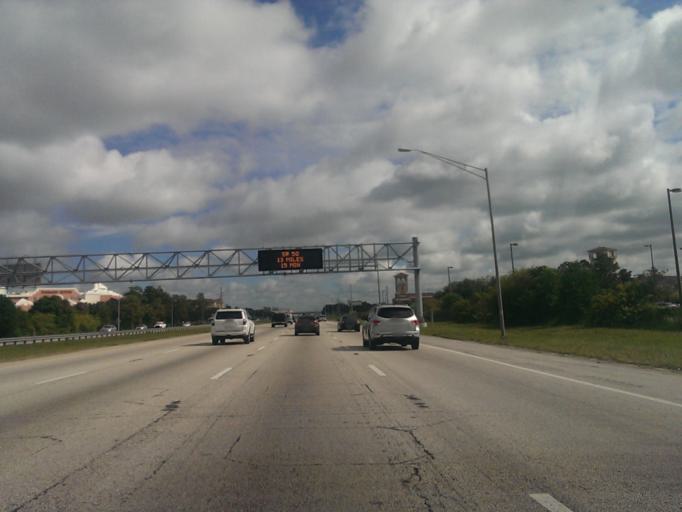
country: US
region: Florida
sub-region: Orange County
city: Williamsburg
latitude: 28.3873
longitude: -81.4956
